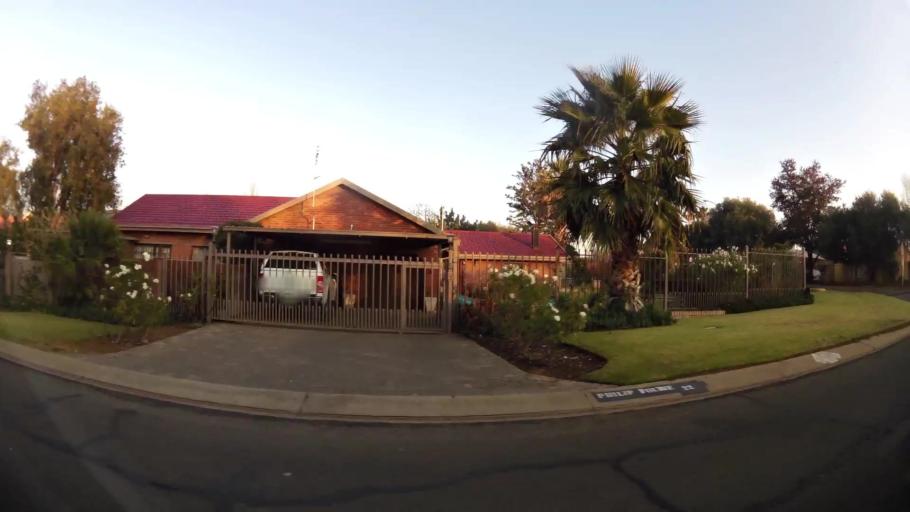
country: ZA
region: Orange Free State
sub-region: Mangaung Metropolitan Municipality
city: Bloemfontein
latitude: -29.1026
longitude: 26.1496
